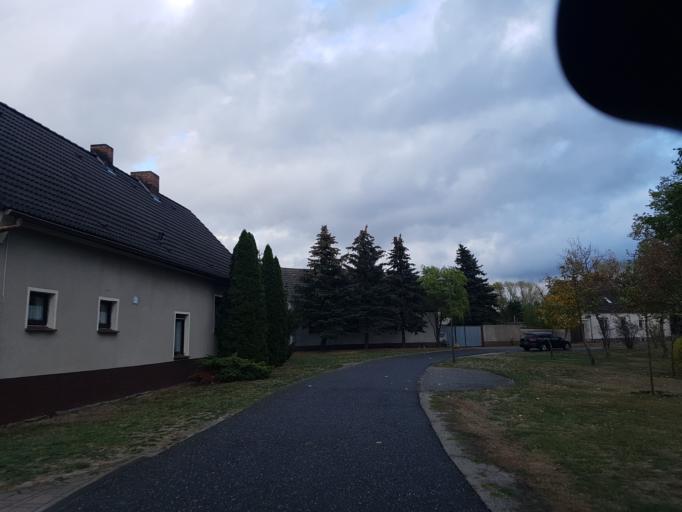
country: DE
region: Saxony-Anhalt
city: Seyda
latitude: 51.8503
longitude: 12.9016
